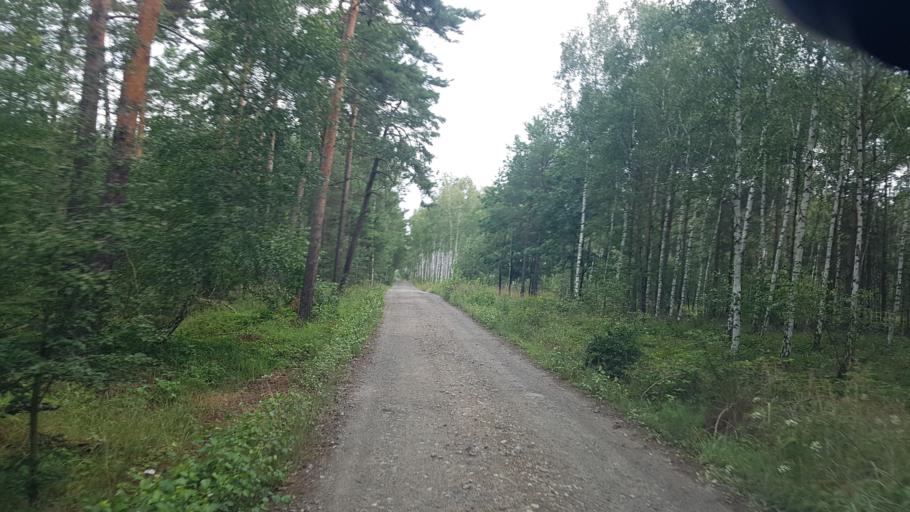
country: DE
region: Brandenburg
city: Grossraschen
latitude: 51.6010
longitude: 13.9571
